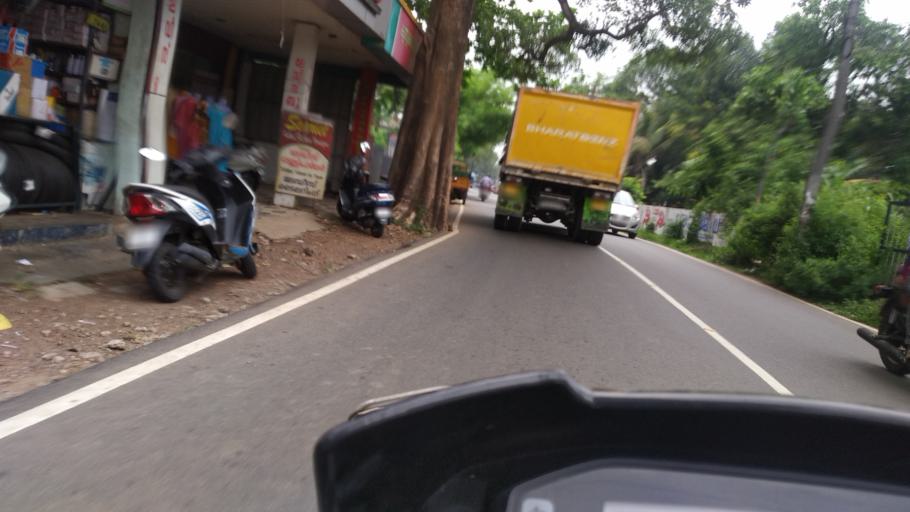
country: IN
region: Kerala
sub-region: Ernakulam
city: Aluva
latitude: 10.1548
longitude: 76.2937
